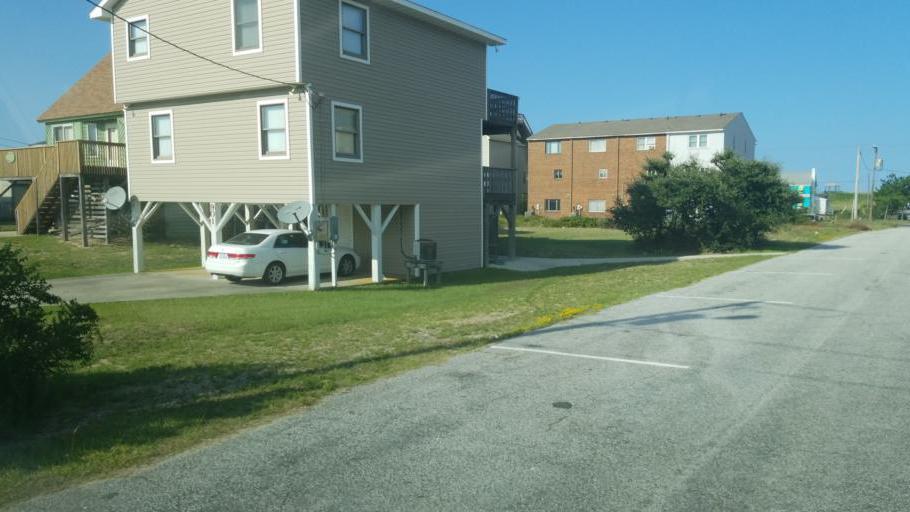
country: US
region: North Carolina
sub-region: Dare County
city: Kill Devil Hills
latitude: 36.0194
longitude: -75.6618
